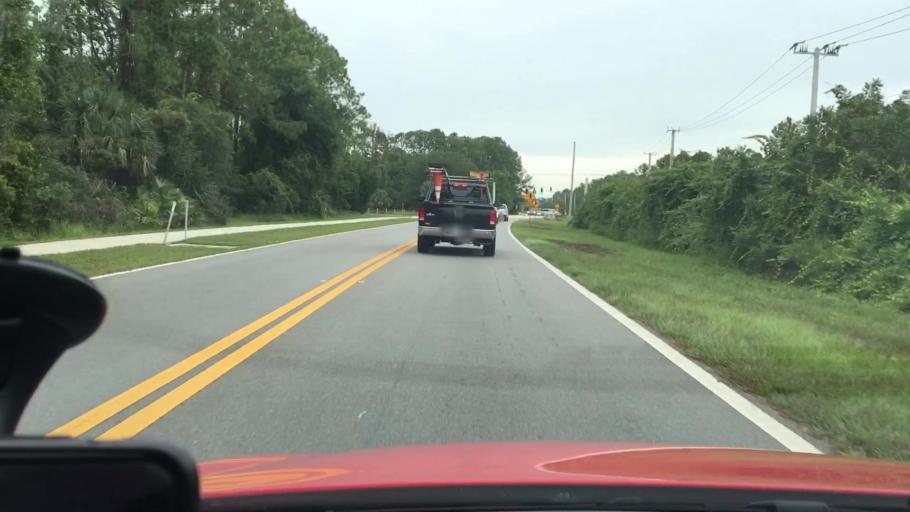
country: US
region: Florida
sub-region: Flagler County
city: Flagler Beach
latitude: 29.4989
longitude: -81.1903
